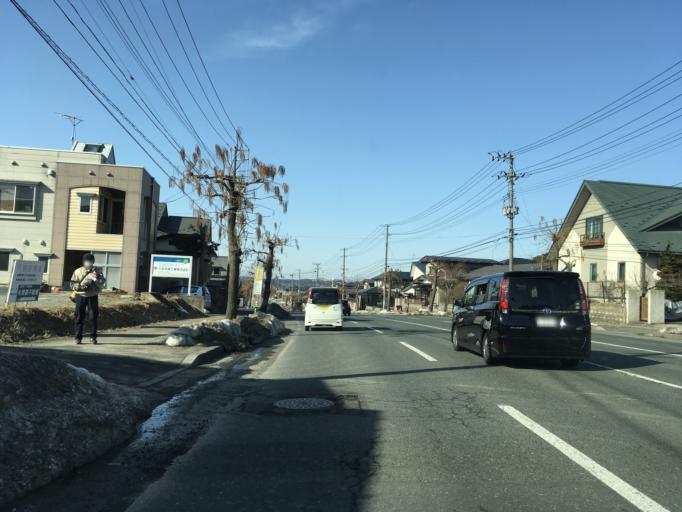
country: JP
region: Iwate
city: Morioka-shi
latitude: 39.7455
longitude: 141.1681
